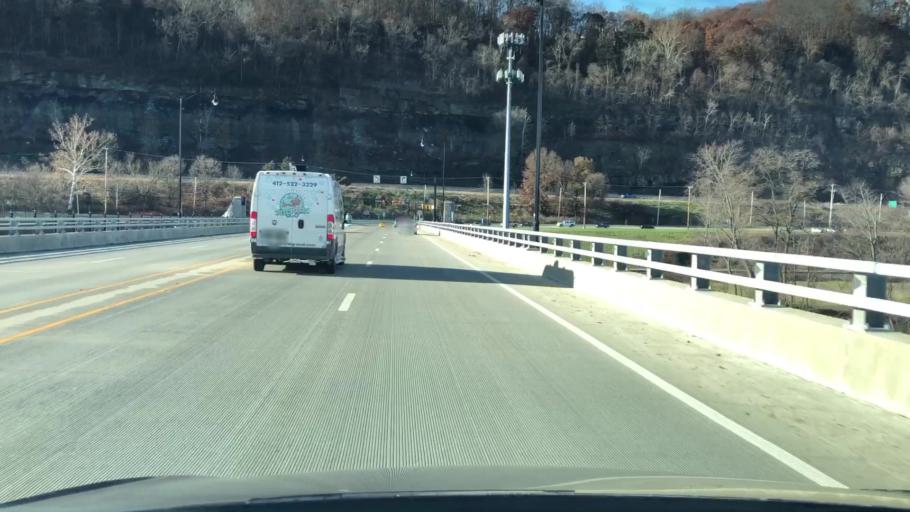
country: US
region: Pennsylvania
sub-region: Allegheny County
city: Oakmont
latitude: 40.5279
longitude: -79.8476
